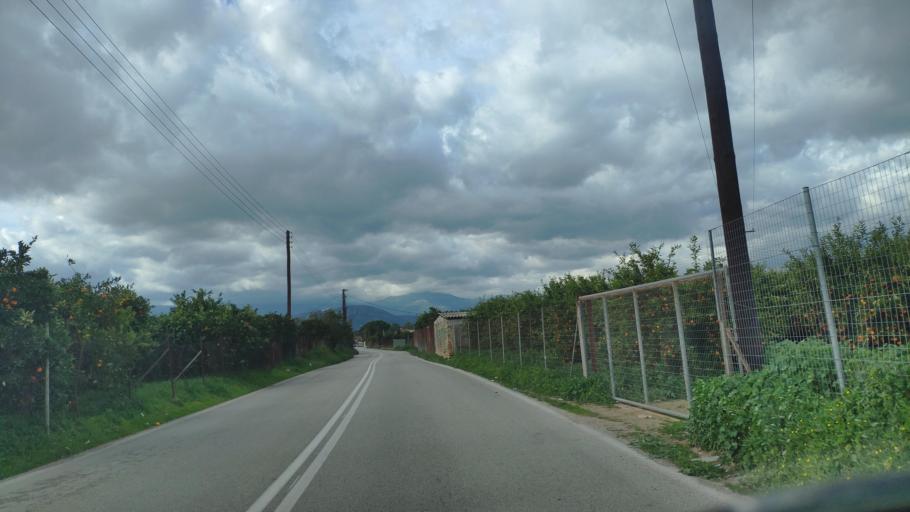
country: GR
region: Peloponnese
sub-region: Nomos Argolidos
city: Nea Tirins
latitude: 37.6084
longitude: 22.8043
